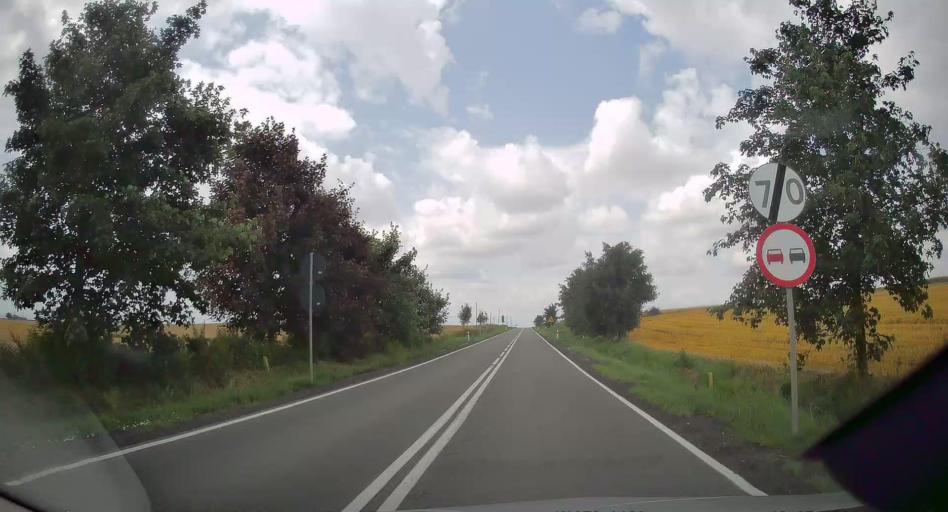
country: PL
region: Opole Voivodeship
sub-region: Powiat prudnicki
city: Raclawice Slaskie
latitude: 50.3529
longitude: 17.8036
